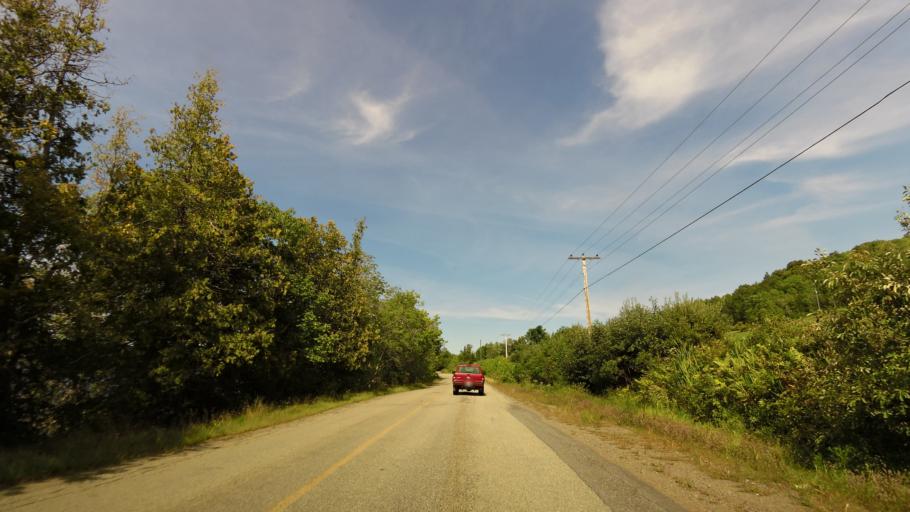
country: CA
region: New Brunswick
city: Hampton
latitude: 45.5980
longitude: -65.9127
